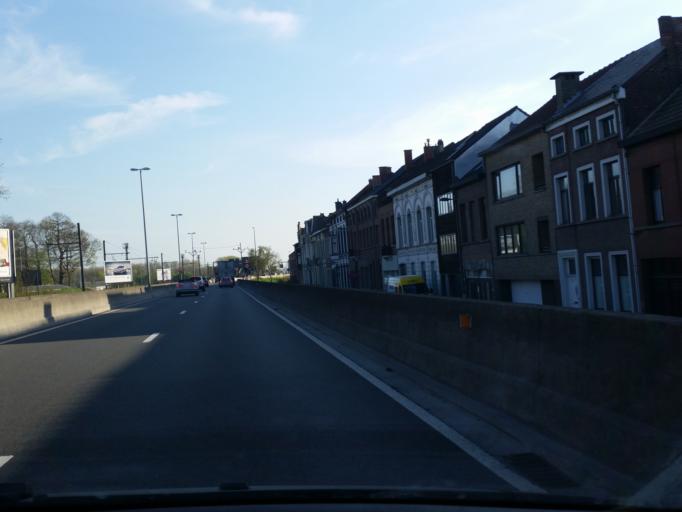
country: BE
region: Flanders
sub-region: Provincie Oost-Vlaanderen
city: Temse
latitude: 51.1259
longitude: 4.2207
